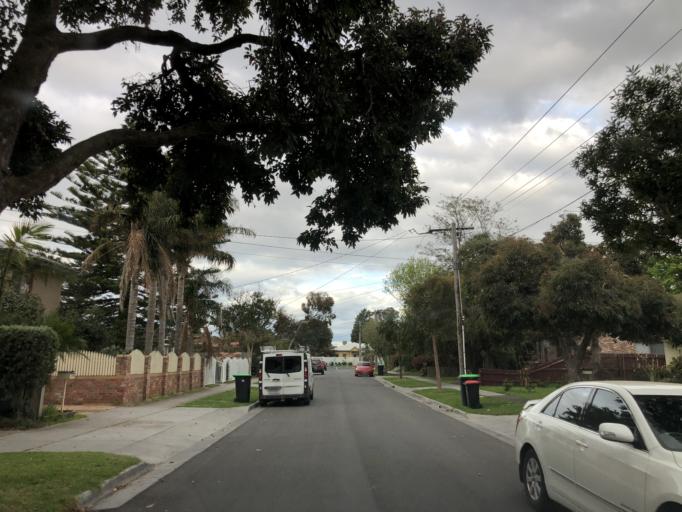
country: AU
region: Victoria
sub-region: Kingston
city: Bonbeach
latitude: -38.0603
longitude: 145.1304
